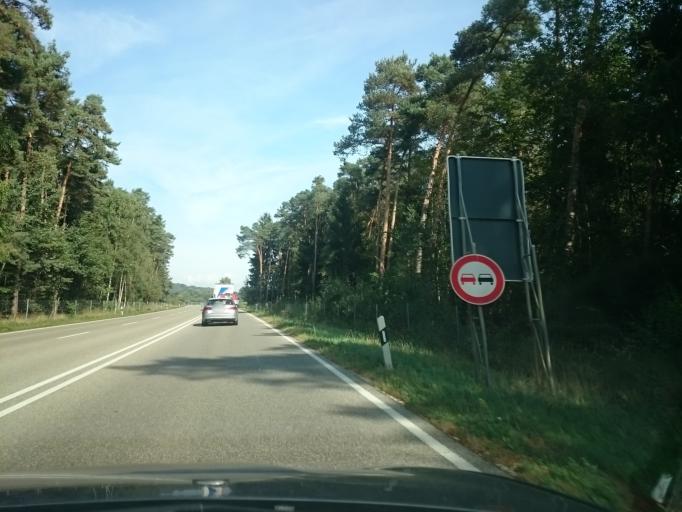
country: DE
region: Bavaria
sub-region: Upper Bavaria
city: Pornbach
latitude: 48.6176
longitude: 11.4411
